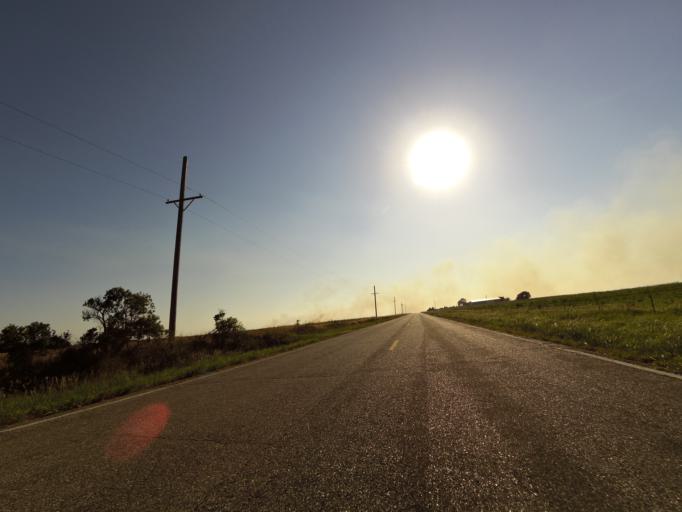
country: US
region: Kansas
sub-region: McPherson County
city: Moundridge
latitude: 38.1451
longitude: -97.5439
